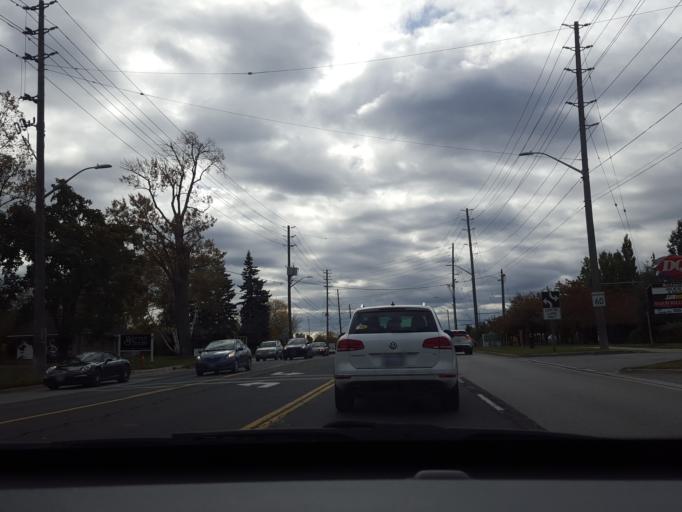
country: CA
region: Ontario
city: Markham
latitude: 43.8427
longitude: -79.3048
